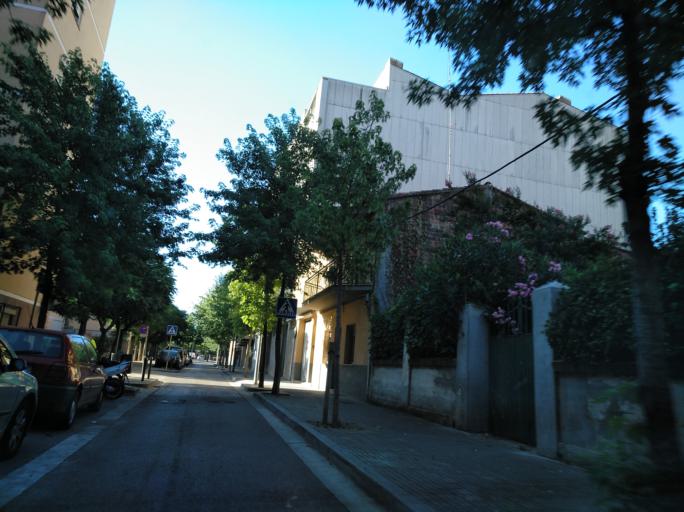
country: ES
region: Catalonia
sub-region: Provincia de Girona
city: Salt
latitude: 41.9725
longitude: 2.7850
